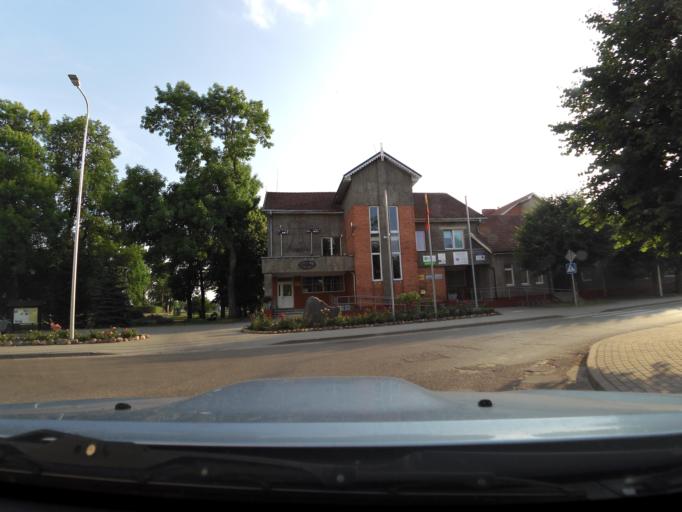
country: LT
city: Rusne
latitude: 55.2965
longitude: 21.3777
